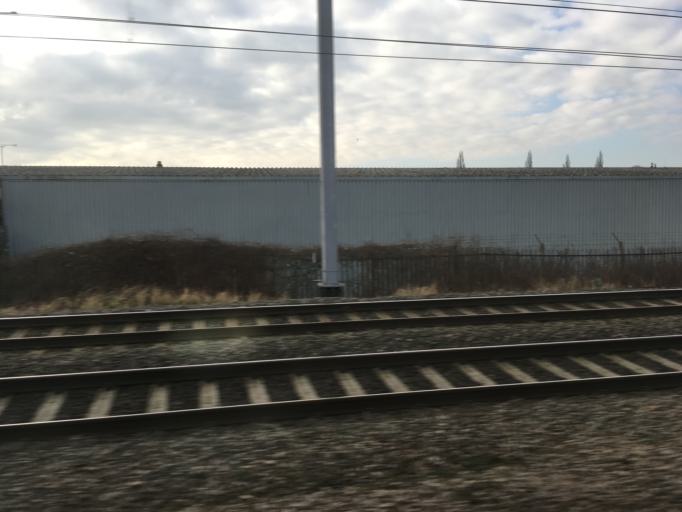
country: GB
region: England
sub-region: West Berkshire
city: Tilehurst
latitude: 51.4652
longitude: -1.0147
